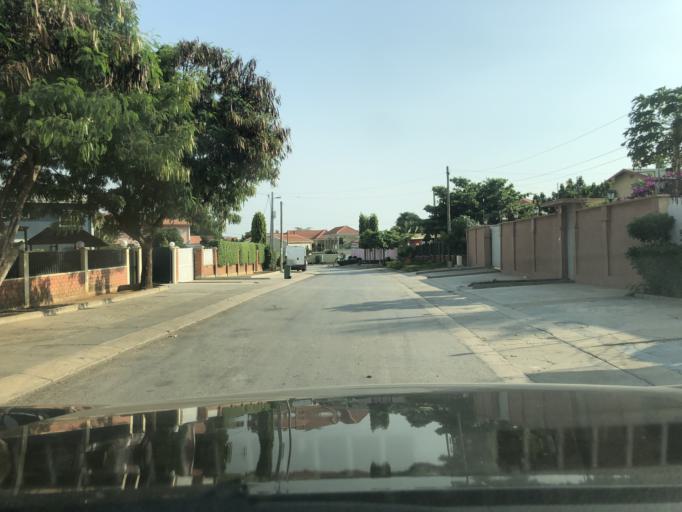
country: AO
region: Luanda
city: Luanda
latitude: -8.9082
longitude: 13.2273
